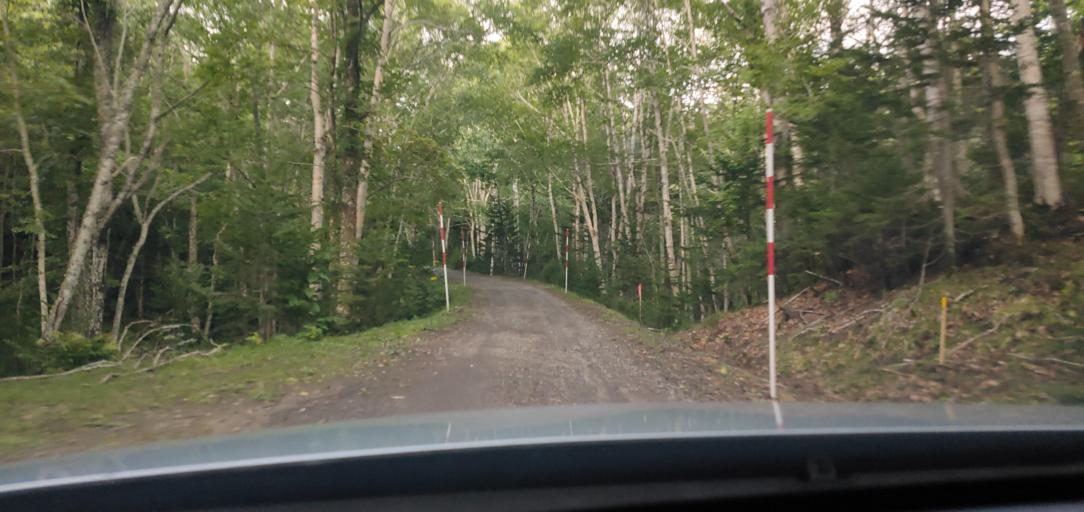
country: JP
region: Hokkaido
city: Kitami
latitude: 43.3742
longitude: 143.9664
